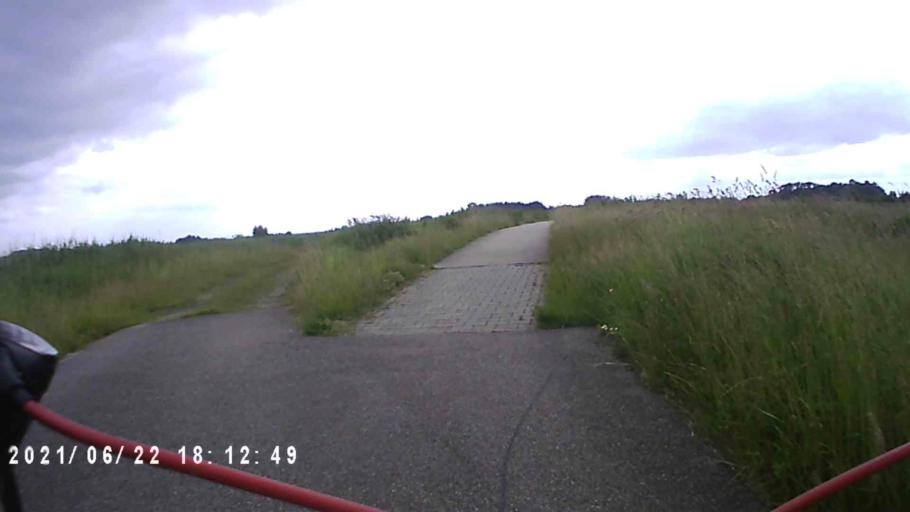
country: NL
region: Groningen
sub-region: Gemeente Zuidhorn
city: Aduard
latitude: 53.1748
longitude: 6.4890
